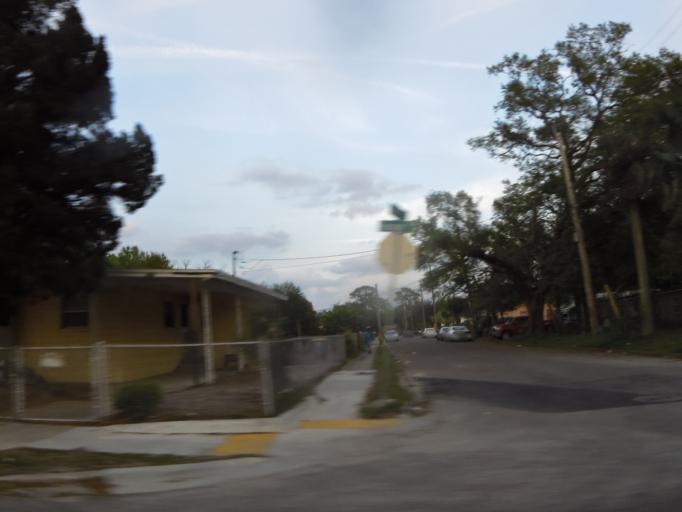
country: US
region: Florida
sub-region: Duval County
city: Jacksonville
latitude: 30.3607
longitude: -81.6328
